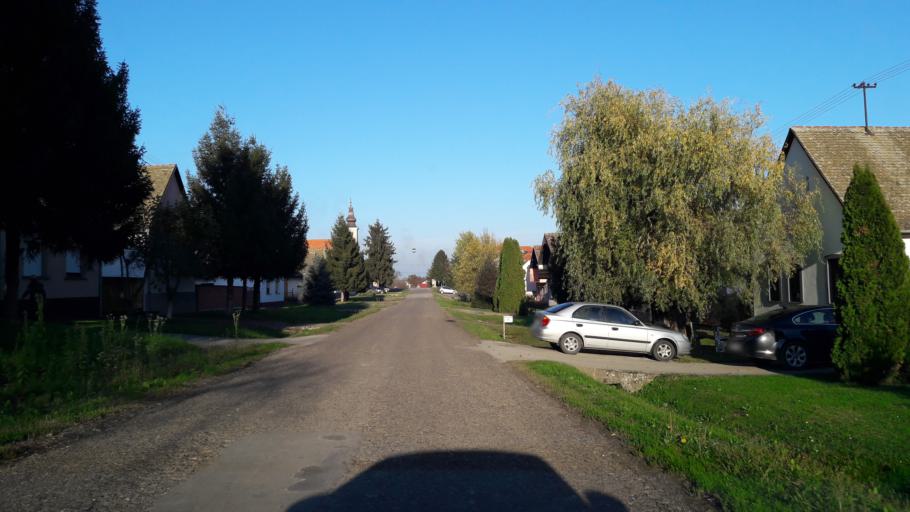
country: HR
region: Osjecko-Baranjska
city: Viskovci
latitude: 45.3416
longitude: 18.4543
